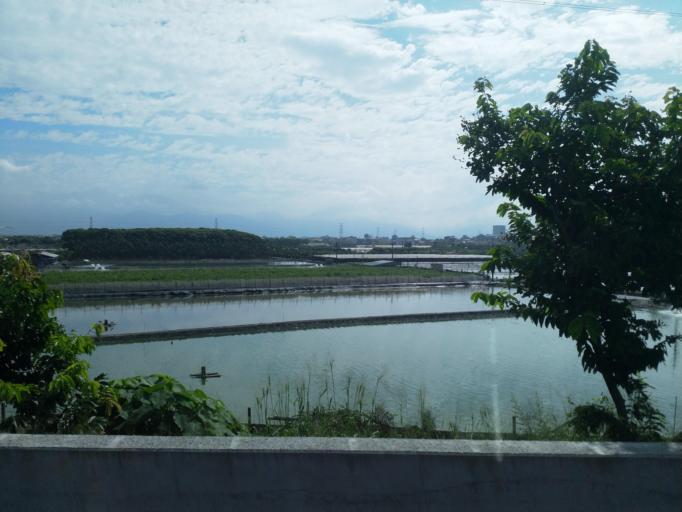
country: TW
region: Taiwan
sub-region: Pingtung
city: Pingtung
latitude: 22.8115
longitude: 120.4853
